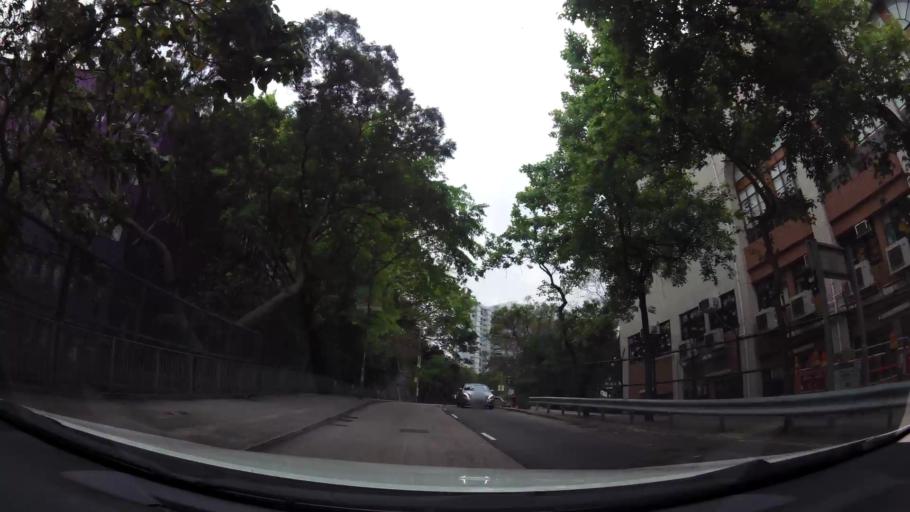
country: HK
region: Wanchai
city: Wan Chai
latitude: 22.2814
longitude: 114.2315
